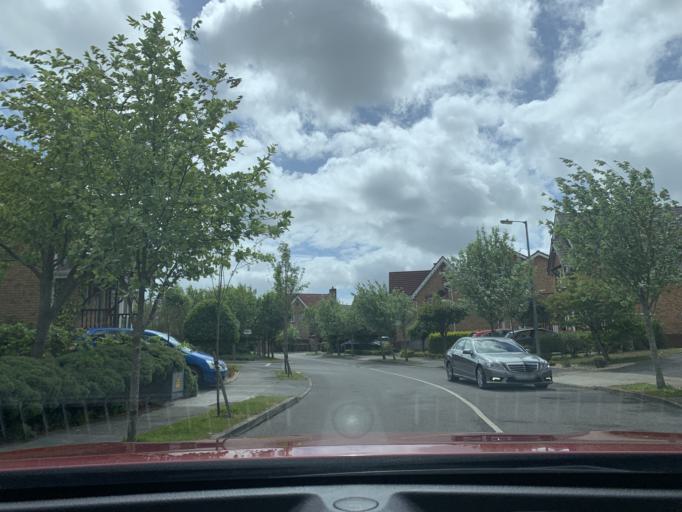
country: IE
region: Connaught
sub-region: Sligo
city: Sligo
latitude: 54.2747
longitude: -8.5130
